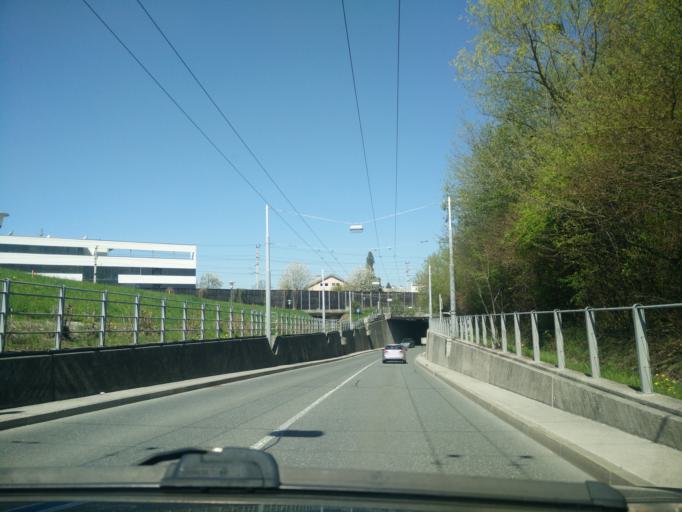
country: AT
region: Salzburg
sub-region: Politischer Bezirk Salzburg-Umgebung
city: Elsbethen
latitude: 47.7770
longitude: 13.0818
